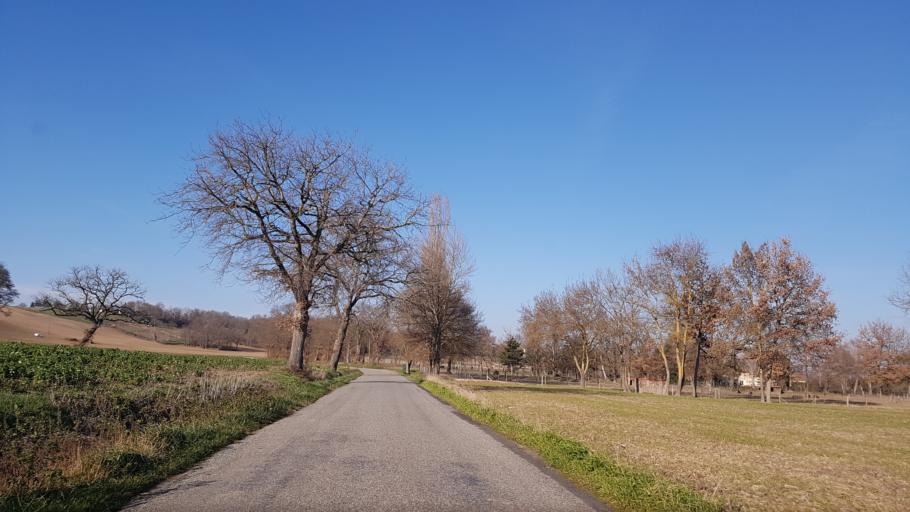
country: FR
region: Midi-Pyrenees
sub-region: Departement de l'Ariege
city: La Tour-du-Crieu
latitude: 43.1297
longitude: 1.7174
